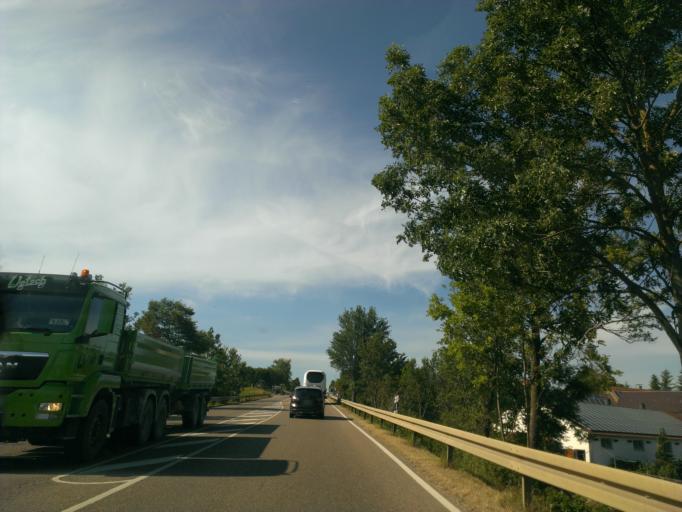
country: DE
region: Bavaria
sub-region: Swabia
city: Marktoffingen
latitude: 48.9220
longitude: 10.4658
